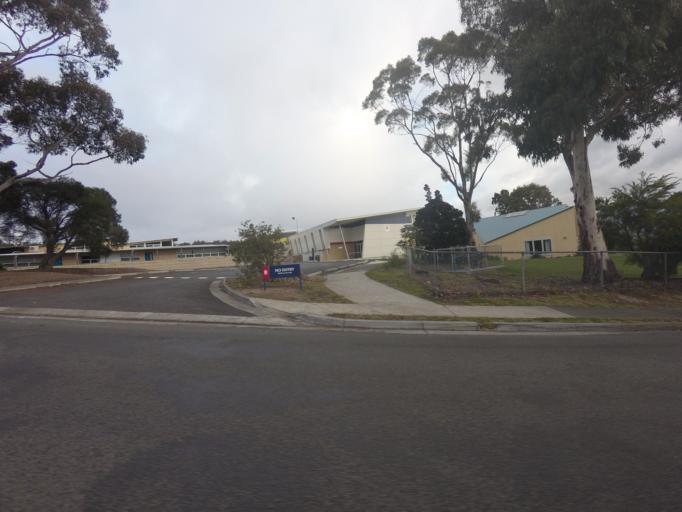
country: AU
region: Tasmania
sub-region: Clarence
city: Warrane
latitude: -42.8571
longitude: 147.4008
